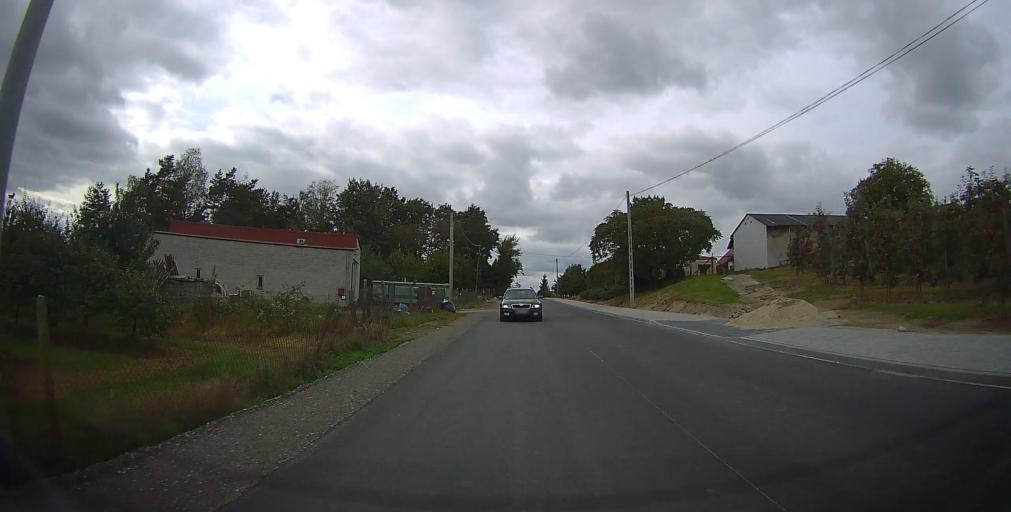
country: PL
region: Masovian Voivodeship
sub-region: Powiat grojecki
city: Belsk Duzy
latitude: 51.8133
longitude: 20.8325
